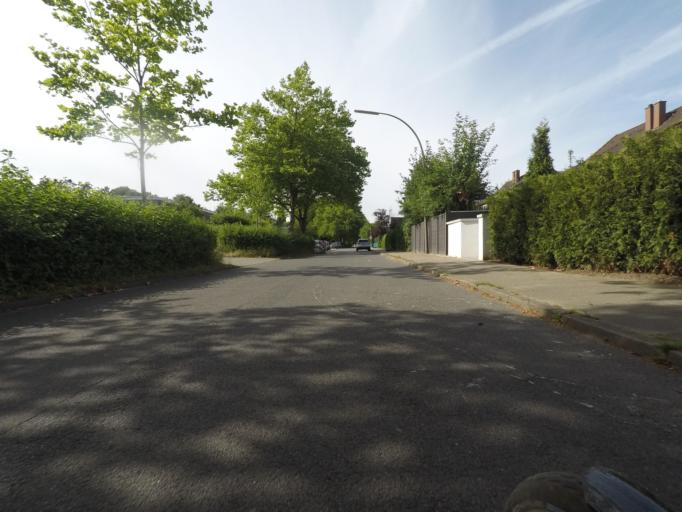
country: DE
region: Hamburg
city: Sasel
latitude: 53.6490
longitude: 10.1115
